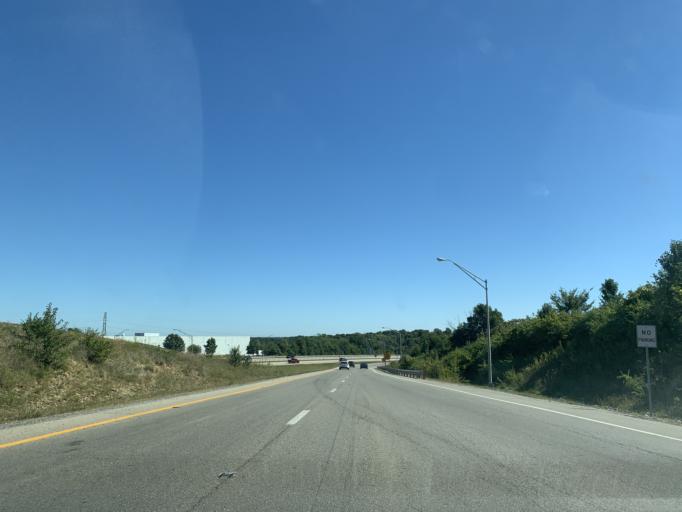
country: US
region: Kentucky
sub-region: Boone County
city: Hebron
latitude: 39.0804
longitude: -84.7069
